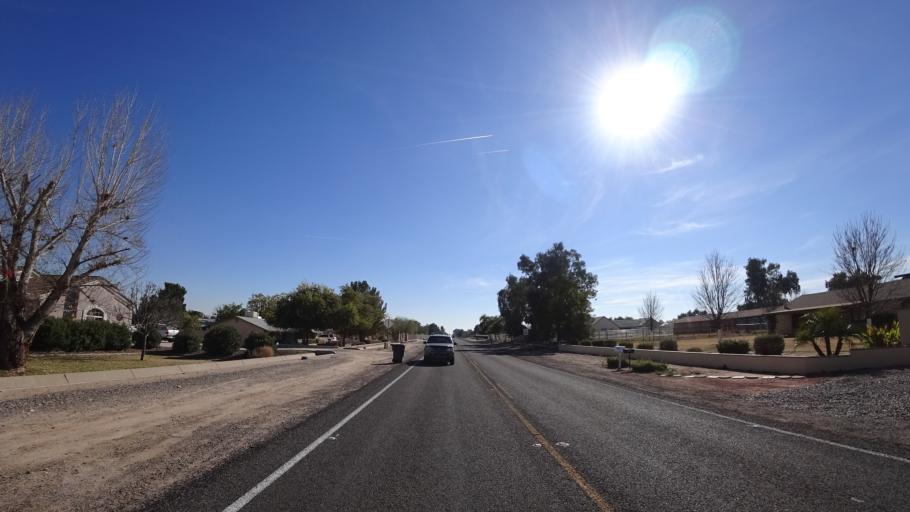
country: US
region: Arizona
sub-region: Maricopa County
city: Citrus Park
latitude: 33.5508
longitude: -112.4443
